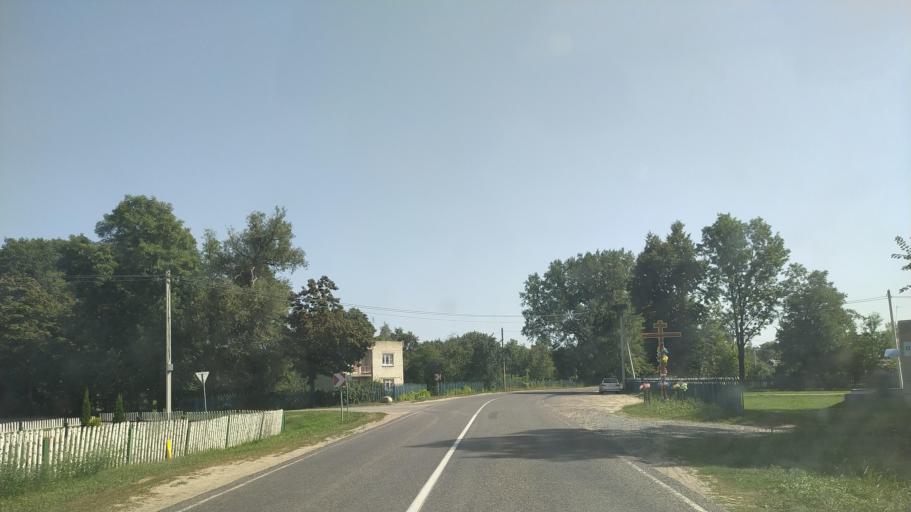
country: BY
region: Brest
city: Byaroza
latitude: 52.3914
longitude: 25.0152
